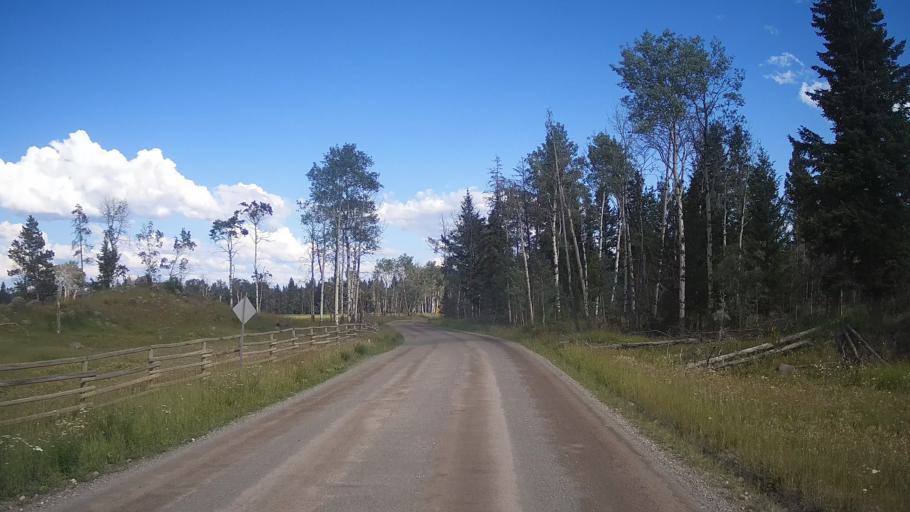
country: CA
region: British Columbia
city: Cache Creek
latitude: 51.1802
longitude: -121.5796
